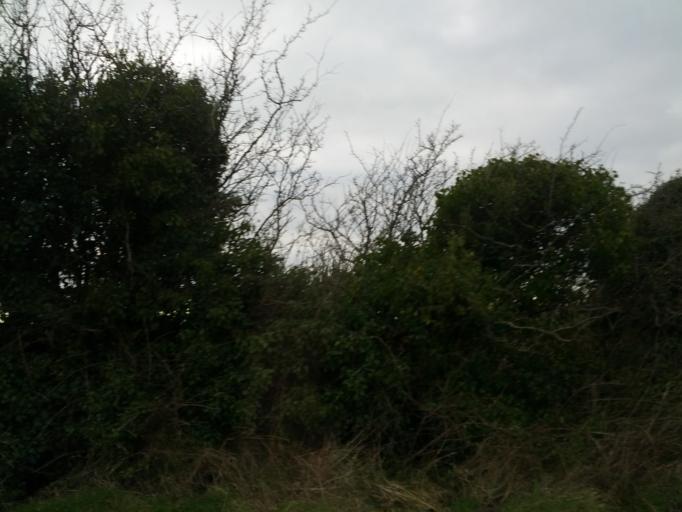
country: IE
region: Connaught
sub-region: County Galway
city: Oranmore
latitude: 53.1912
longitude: -8.9232
